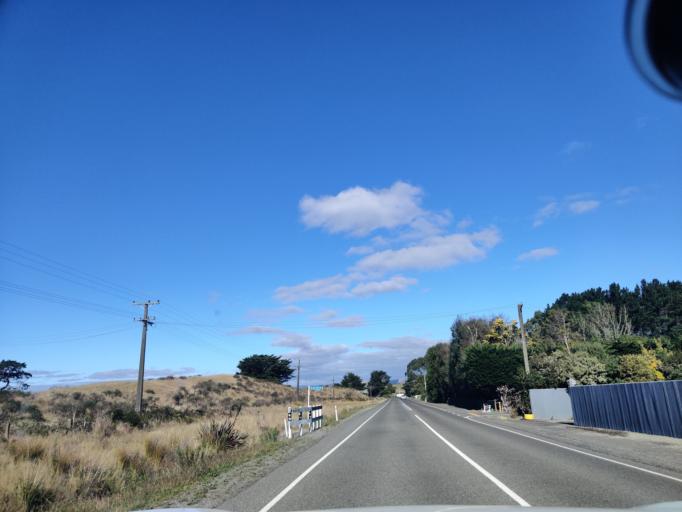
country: NZ
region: Manawatu-Wanganui
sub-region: Horowhenua District
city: Foxton
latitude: -40.4211
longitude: 175.4346
